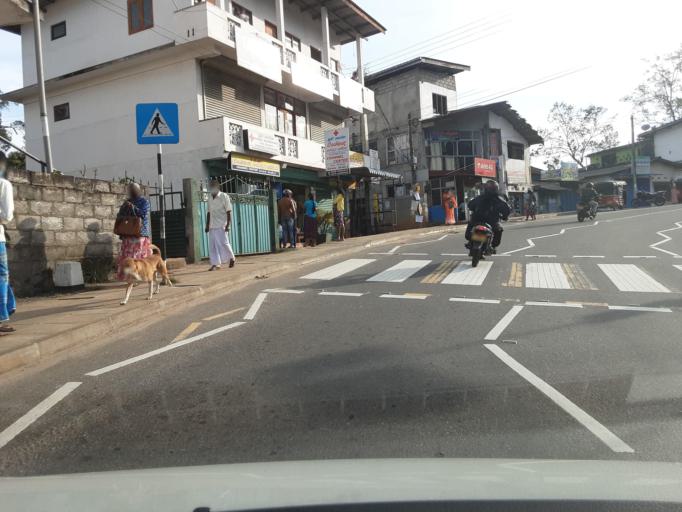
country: LK
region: Uva
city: Badulla
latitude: 6.9371
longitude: 80.9906
